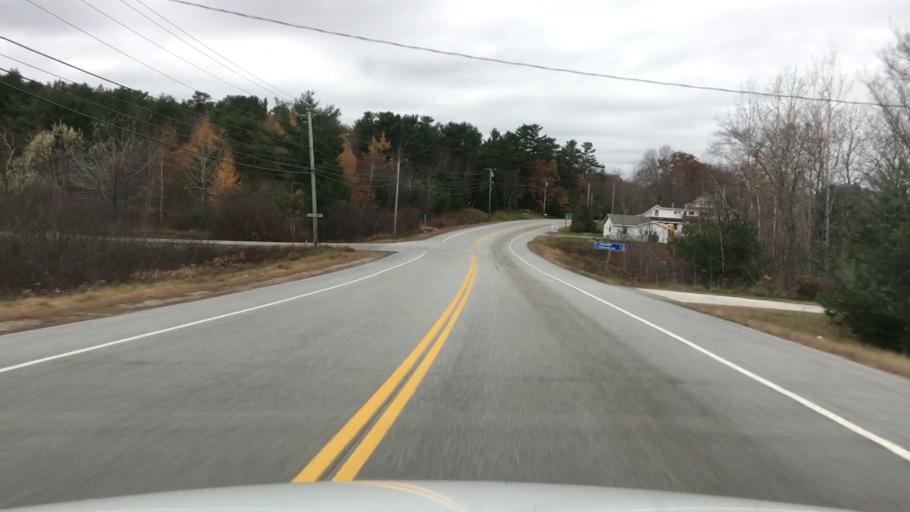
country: US
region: Maine
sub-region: Hancock County
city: Orland
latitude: 44.5587
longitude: -68.7047
